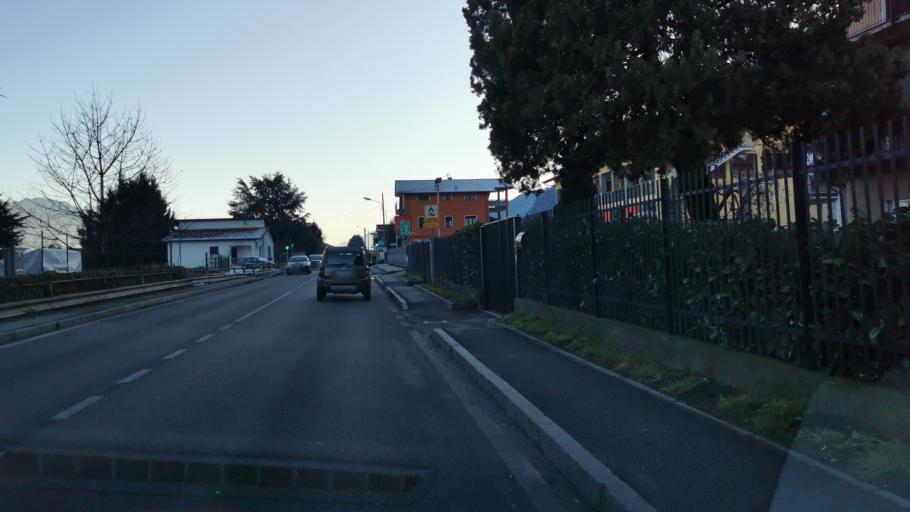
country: IT
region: Lombardy
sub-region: Provincia di Como
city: Dongo
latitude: 46.1331
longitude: 9.2866
